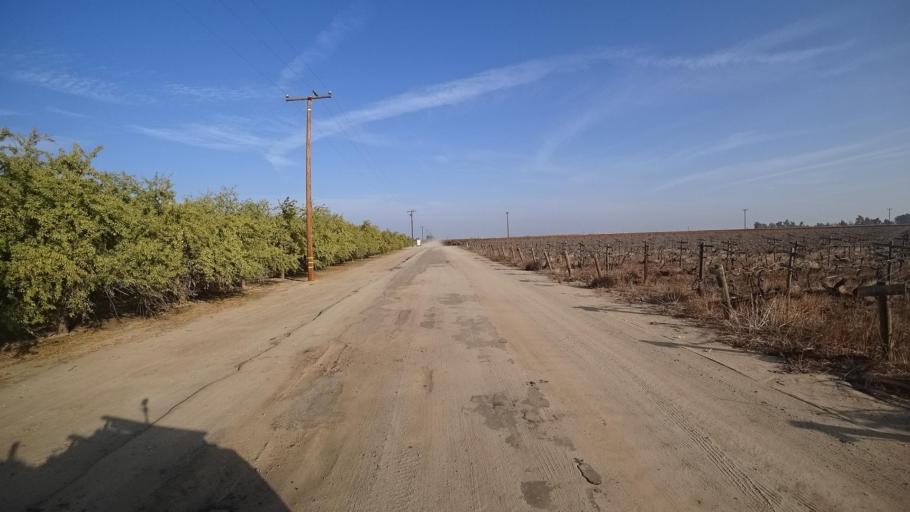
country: US
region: California
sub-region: Kern County
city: Delano
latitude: 35.7387
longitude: -119.1873
